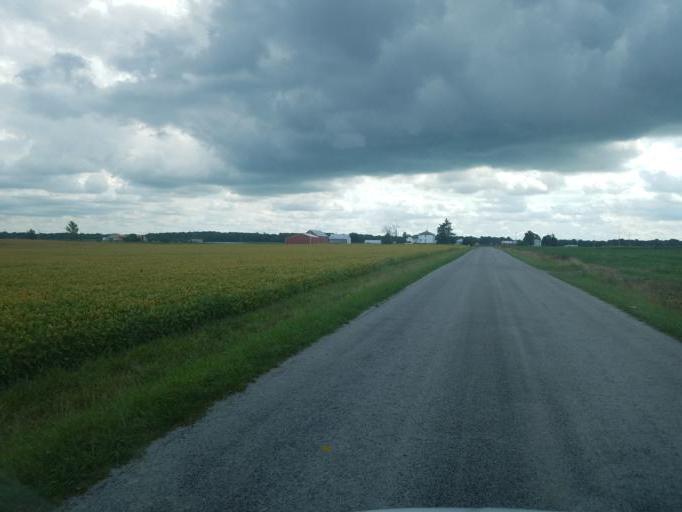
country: US
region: Ohio
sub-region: Huron County
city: Greenwich
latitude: 40.9971
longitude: -82.5344
